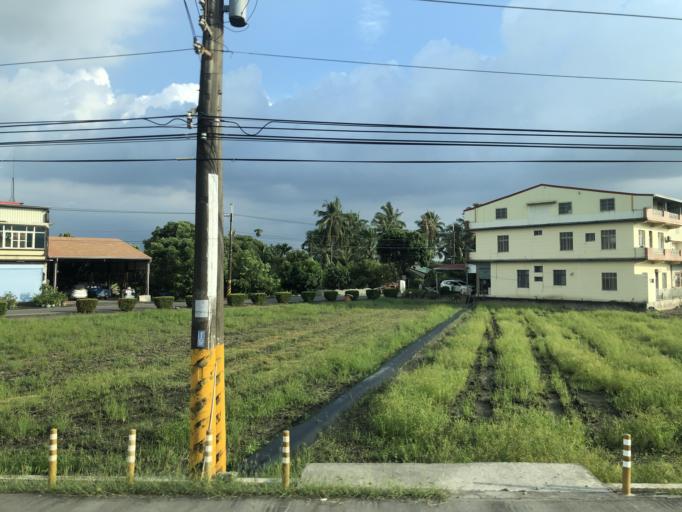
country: TW
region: Taiwan
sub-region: Pingtung
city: Pingtung
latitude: 22.8994
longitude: 120.5251
